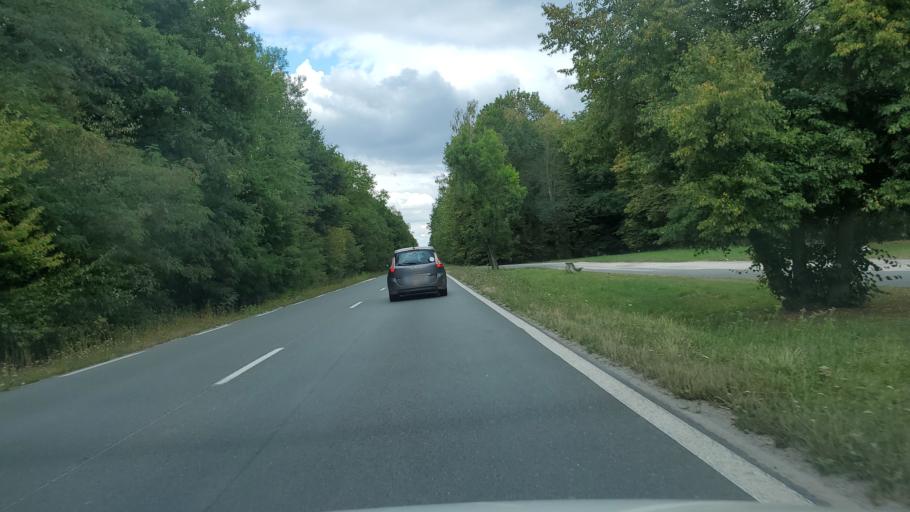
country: FR
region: Ile-de-France
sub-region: Departement de Seine-et-Marne
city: La Houssaye-en-Brie
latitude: 48.7896
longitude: 2.8731
